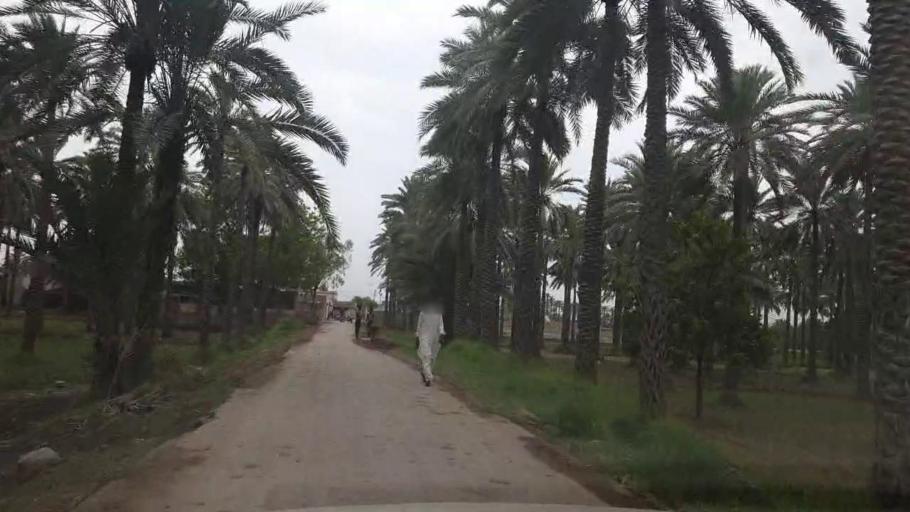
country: PK
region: Sindh
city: Khairpur
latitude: 27.5544
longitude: 68.7506
